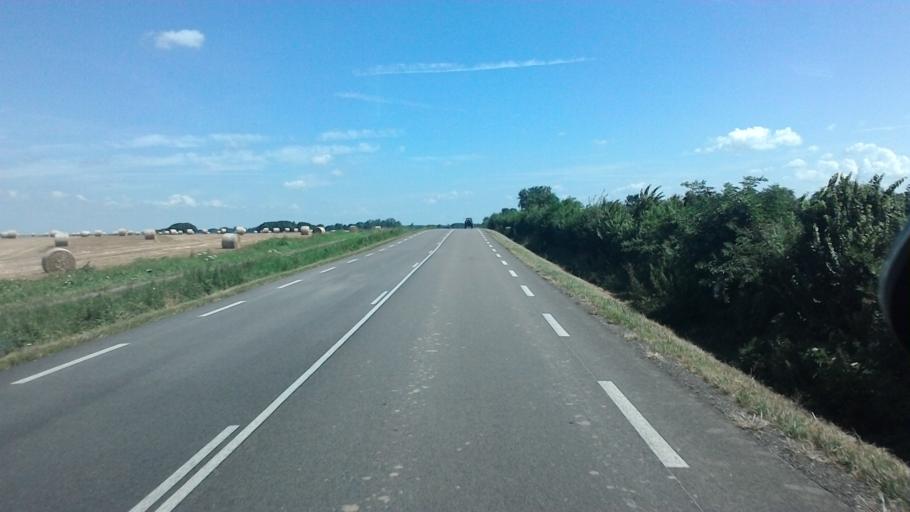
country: FR
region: Bourgogne
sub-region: Departement de la Cote-d'Or
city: Seurre
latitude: 46.9206
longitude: 5.1182
